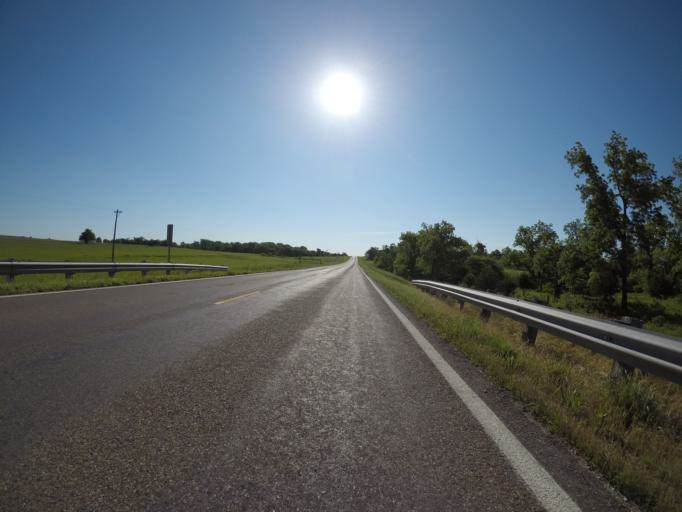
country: US
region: Kansas
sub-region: Lyon County
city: Emporia
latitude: 38.6589
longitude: -96.2249
